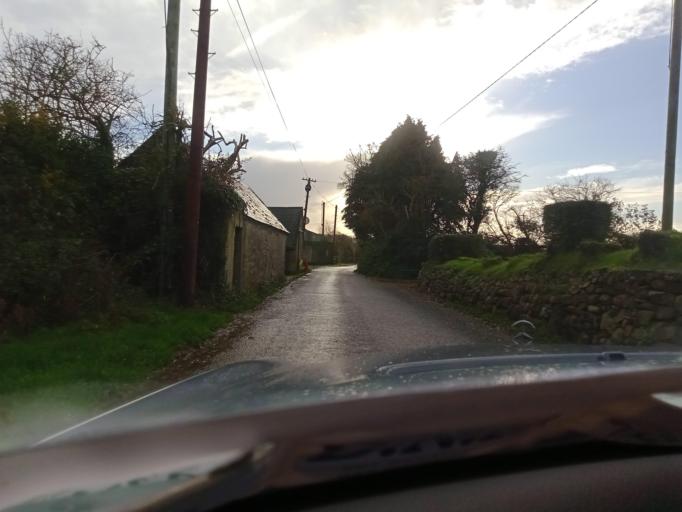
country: IE
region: Leinster
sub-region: Kilkenny
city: Mooncoin
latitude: 52.2761
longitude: -7.1842
